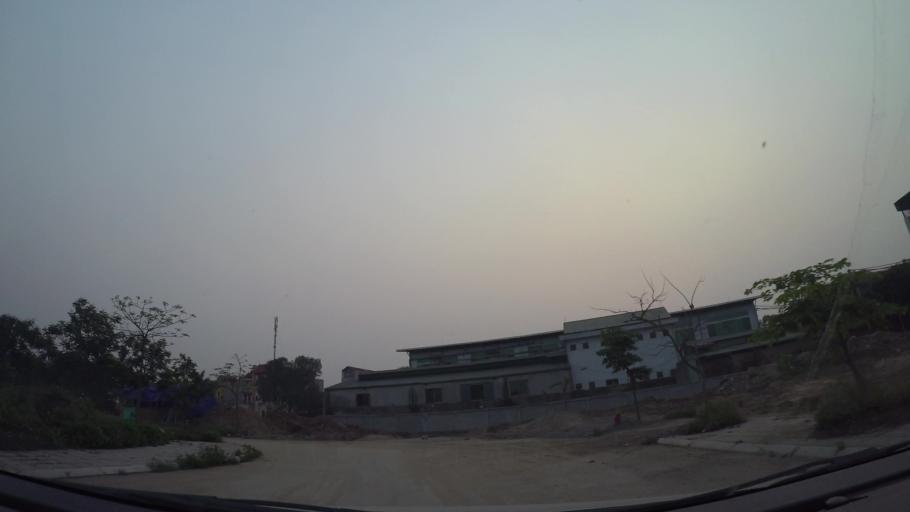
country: VN
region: Ha Noi
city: Ha Dong
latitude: 20.9949
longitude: 105.7308
